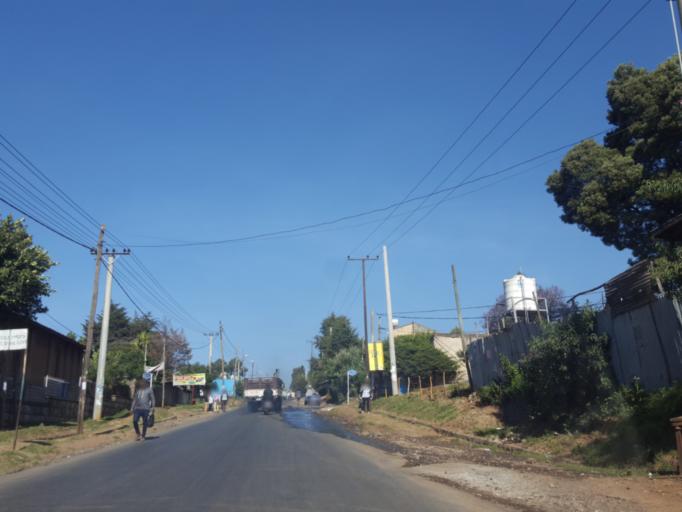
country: ET
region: Adis Abeba
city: Addis Ababa
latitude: 9.0529
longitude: 38.7350
